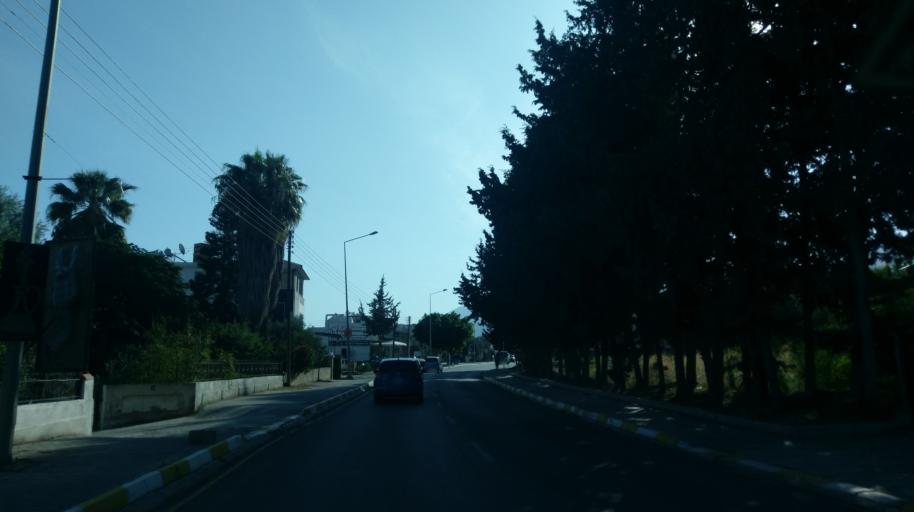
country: CY
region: Keryneia
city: Kyrenia
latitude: 35.3314
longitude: 33.3327
